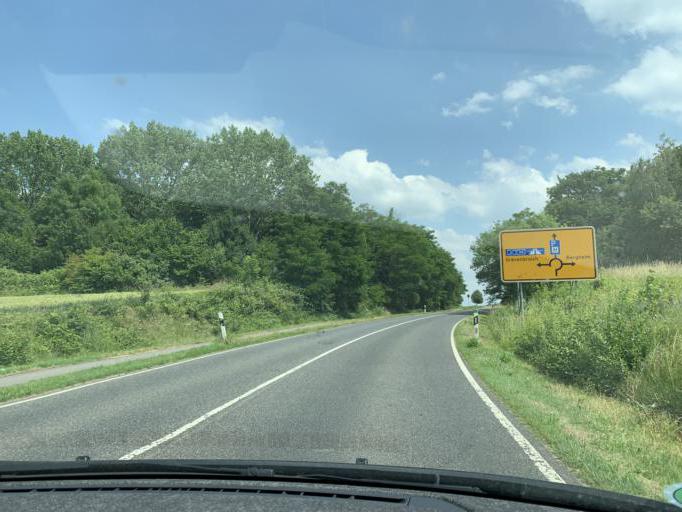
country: DE
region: North Rhine-Westphalia
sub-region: Regierungsbezirk Koln
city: Bedburg
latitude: 50.9930
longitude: 6.5846
